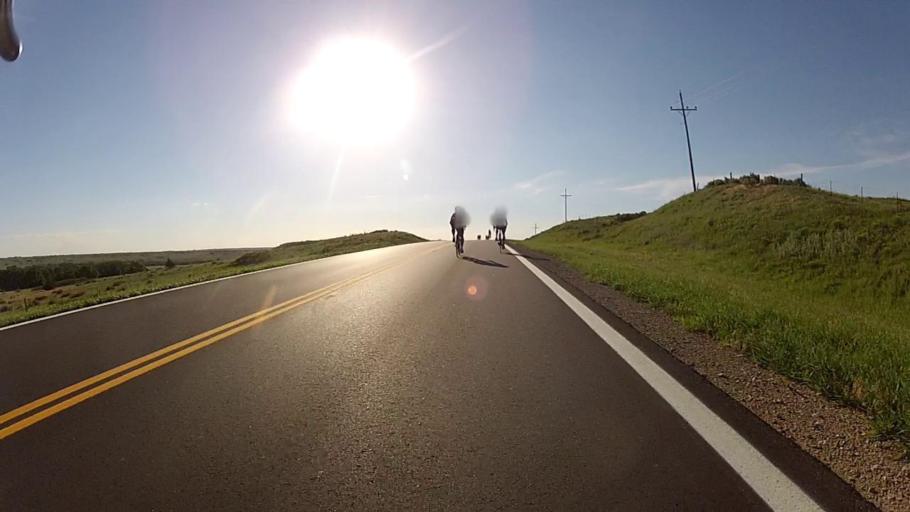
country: US
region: Kansas
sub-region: Comanche County
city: Coldwater
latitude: 37.2817
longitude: -99.0682
